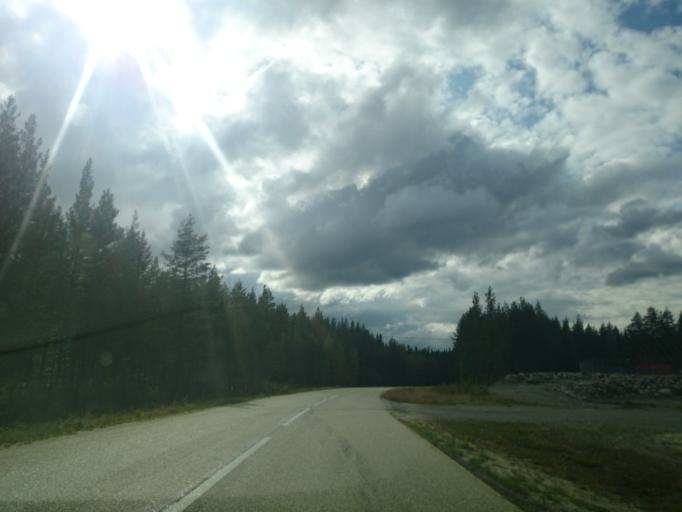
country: SE
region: Jaemtland
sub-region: Harjedalens Kommun
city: Sveg
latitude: 62.4124
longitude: 13.6142
